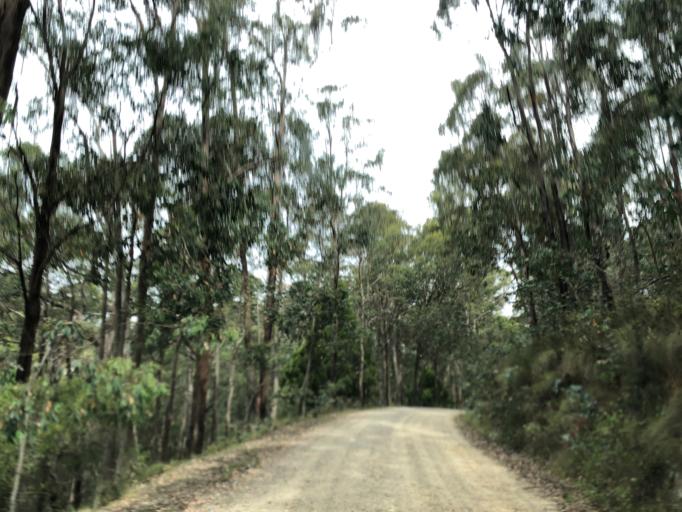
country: AU
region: Victoria
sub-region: Moorabool
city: Bacchus Marsh
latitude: -37.4632
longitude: 144.2769
